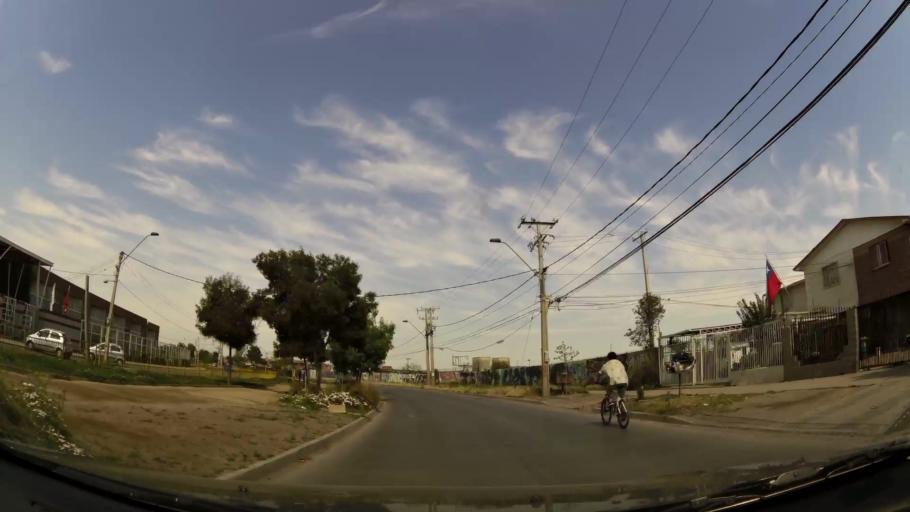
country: CL
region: Santiago Metropolitan
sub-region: Provincia de Santiago
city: La Pintana
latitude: -33.5715
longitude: -70.5992
